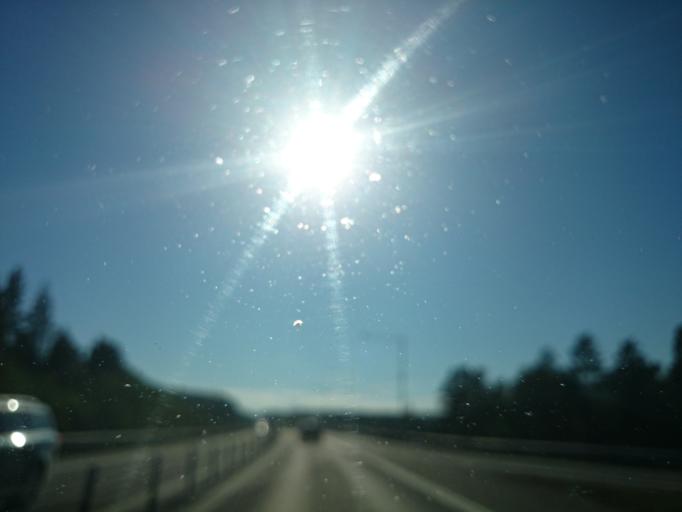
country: SE
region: Vaesternorrland
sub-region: Timra Kommun
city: Bergeforsen
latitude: 62.5182
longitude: 17.4344
